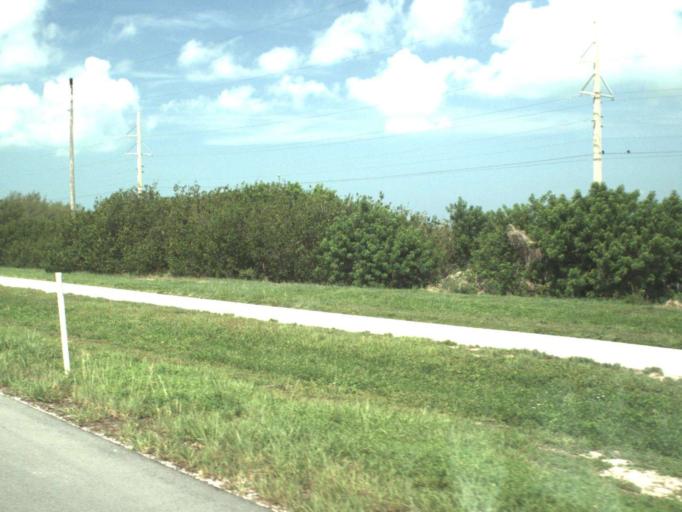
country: US
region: Florida
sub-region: Monroe County
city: Islamorada
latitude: 24.8415
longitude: -80.7534
